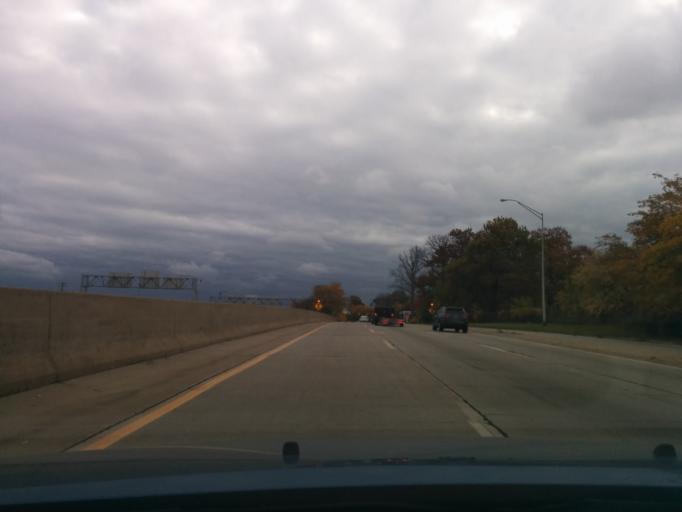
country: US
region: Michigan
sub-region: Wayne County
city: Allen Park
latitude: 42.2657
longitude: -83.2230
